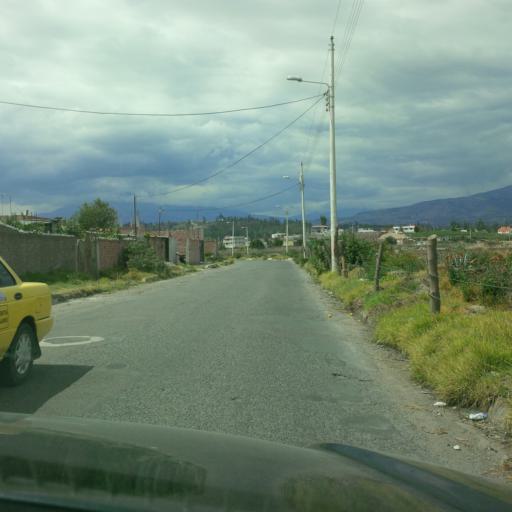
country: EC
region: Chimborazo
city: Riobamba
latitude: -1.6509
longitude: -78.6491
